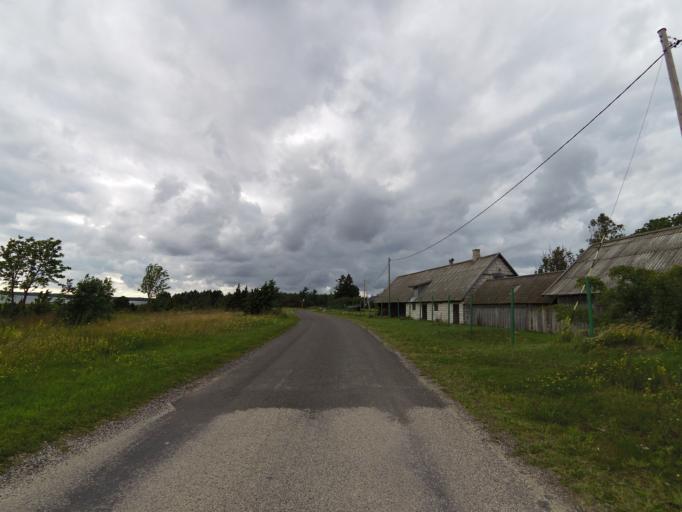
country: EE
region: Laeaene
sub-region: Vormsi vald
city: Hullo
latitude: 58.9721
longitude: 23.2636
